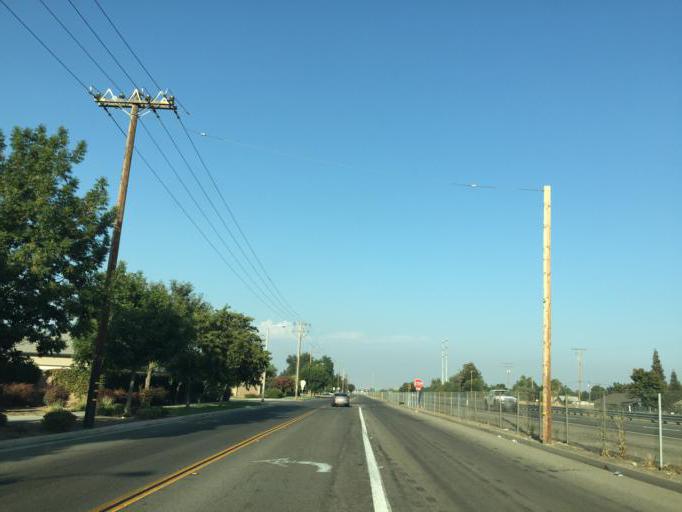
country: US
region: California
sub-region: Tulare County
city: Visalia
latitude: 36.3272
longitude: -119.2484
